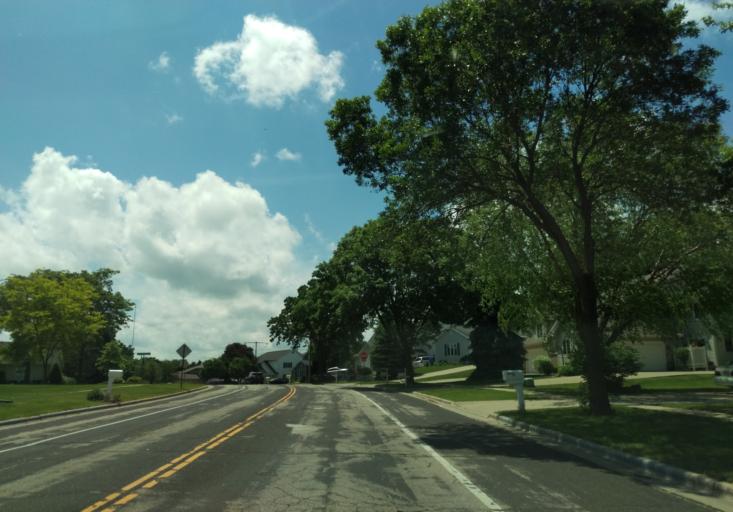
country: US
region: Wisconsin
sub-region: Dane County
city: Middleton
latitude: 43.0861
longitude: -89.5197
